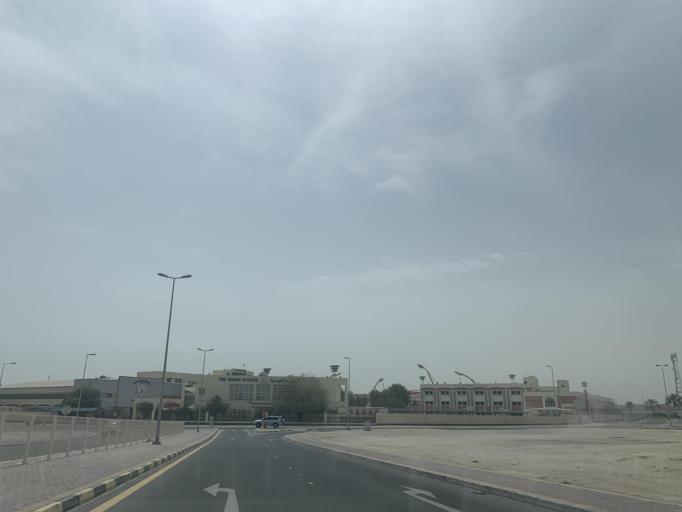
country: BH
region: Northern
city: Madinat `Isa
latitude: 26.1600
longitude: 50.5398
